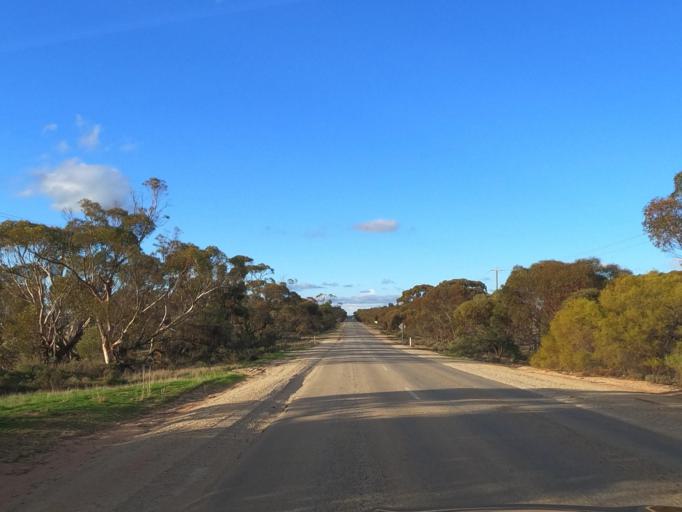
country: AU
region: Victoria
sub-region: Swan Hill
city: Swan Hill
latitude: -35.3486
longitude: 143.5149
